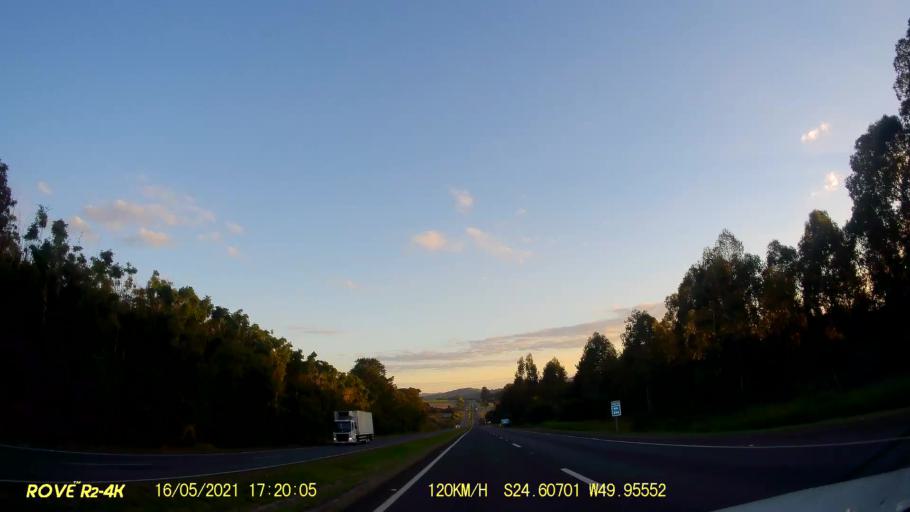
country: BR
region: Parana
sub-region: Pirai Do Sul
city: Pirai do Sul
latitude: -24.6070
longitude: -49.9554
